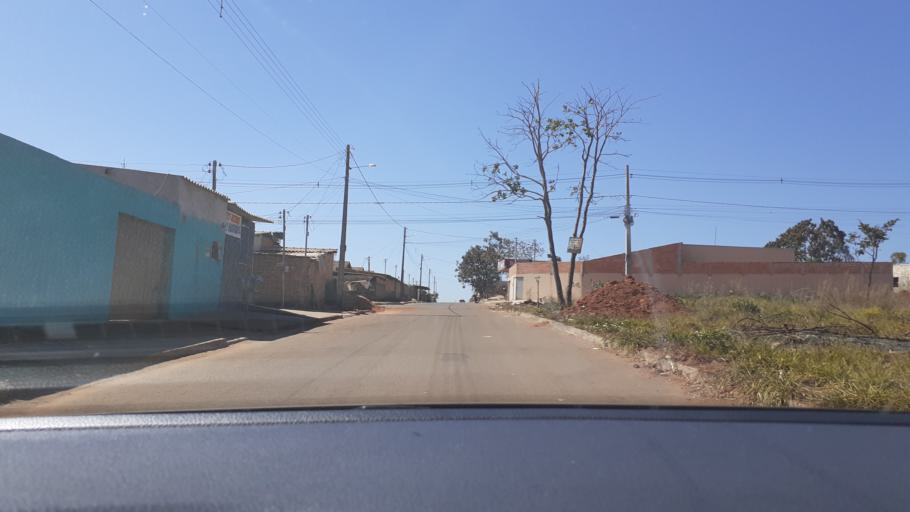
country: BR
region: Goias
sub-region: Aparecida De Goiania
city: Aparecida de Goiania
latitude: -16.8807
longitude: -49.2579
